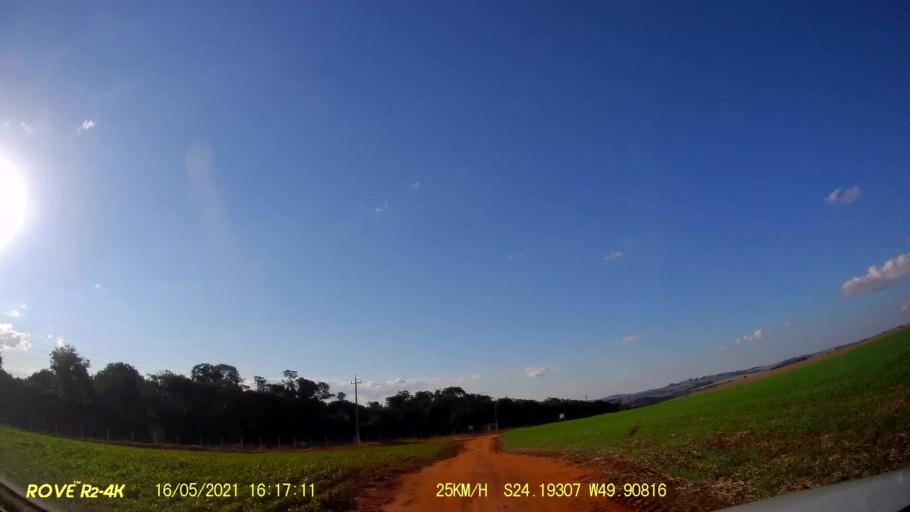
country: BR
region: Parana
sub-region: Jaguariaiva
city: Jaguariaiva
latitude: -24.1929
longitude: -49.9083
